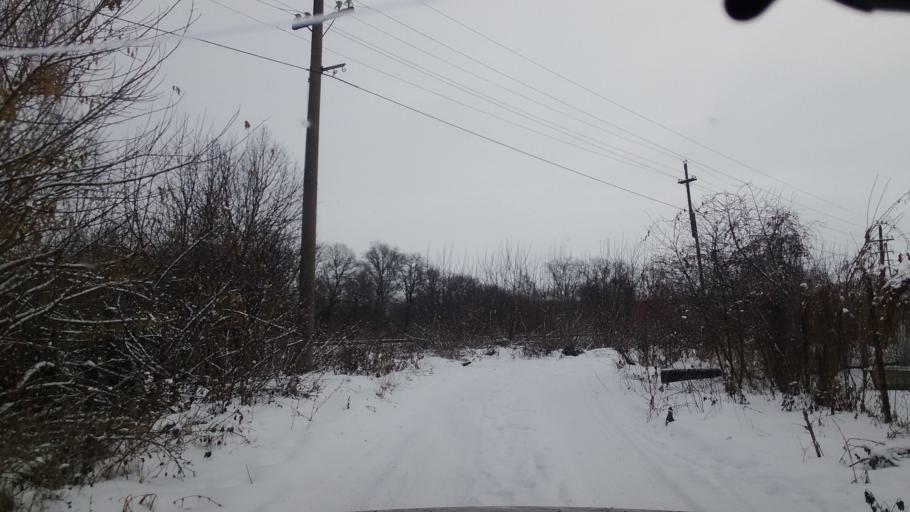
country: RU
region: Tula
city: Bogoroditsk
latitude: 53.7584
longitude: 38.1221
